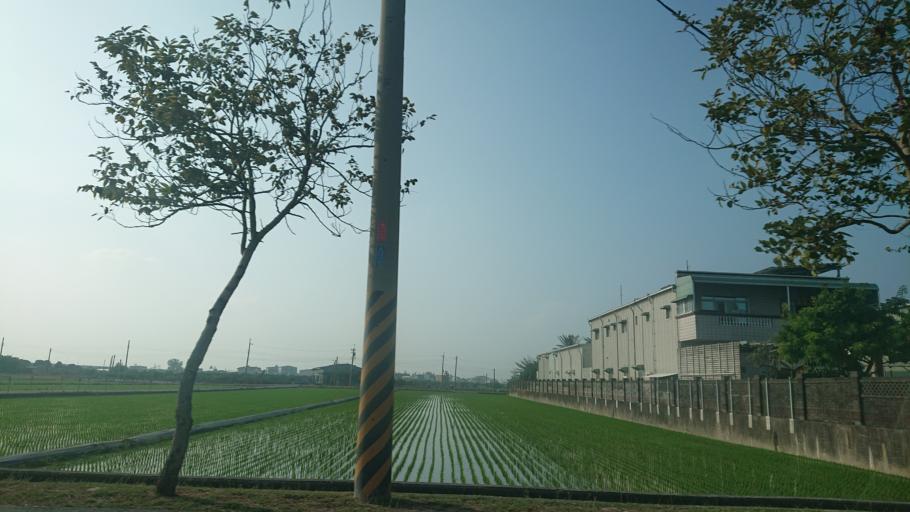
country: TW
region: Taiwan
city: Xinying
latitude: 23.2047
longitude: 120.2711
